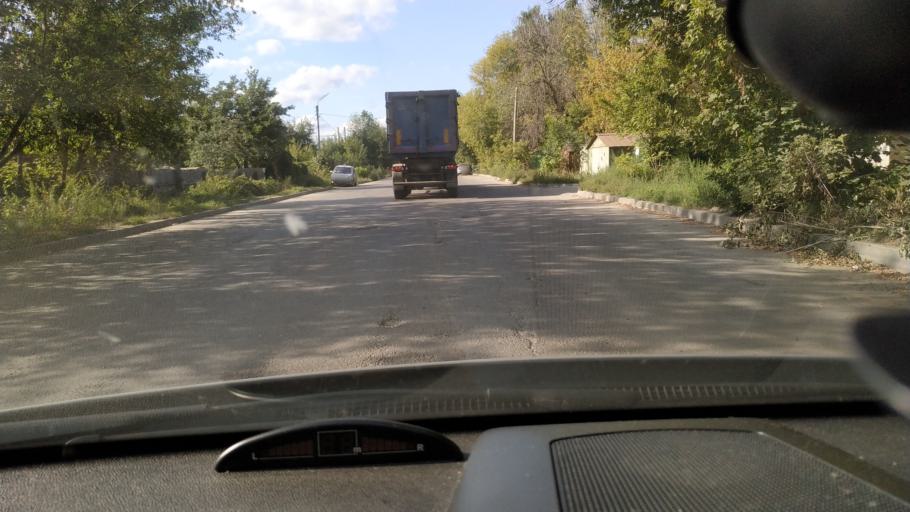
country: RU
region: Rjazan
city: Ryazan'
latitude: 54.6603
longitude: 39.6322
